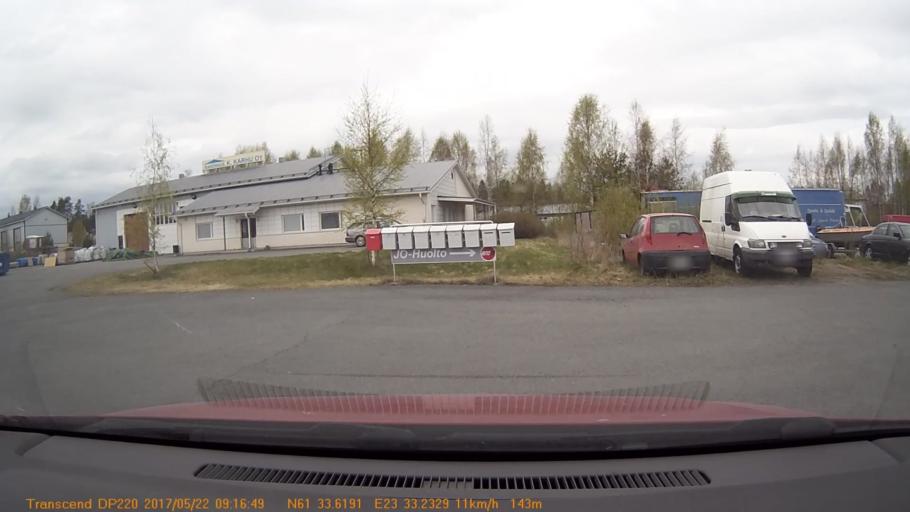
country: FI
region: Pirkanmaa
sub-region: Tampere
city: Yloejaervi
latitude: 61.5602
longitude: 23.5543
